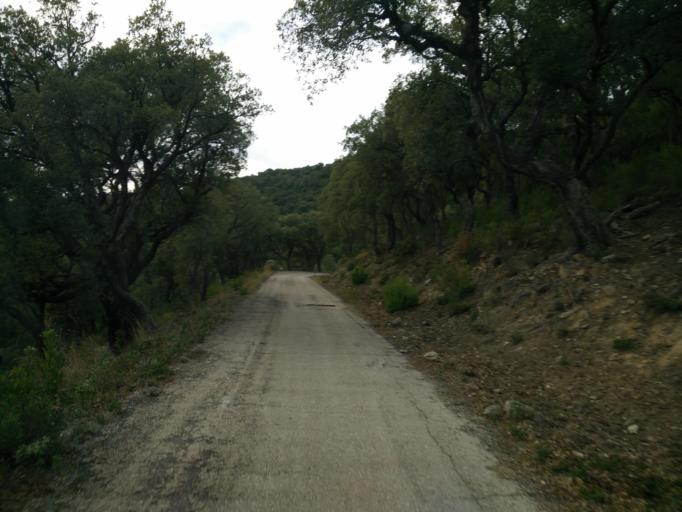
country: FR
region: Provence-Alpes-Cote d'Azur
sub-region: Departement du Var
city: Roquebrune-sur-Argens
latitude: 43.3981
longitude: 6.6178
